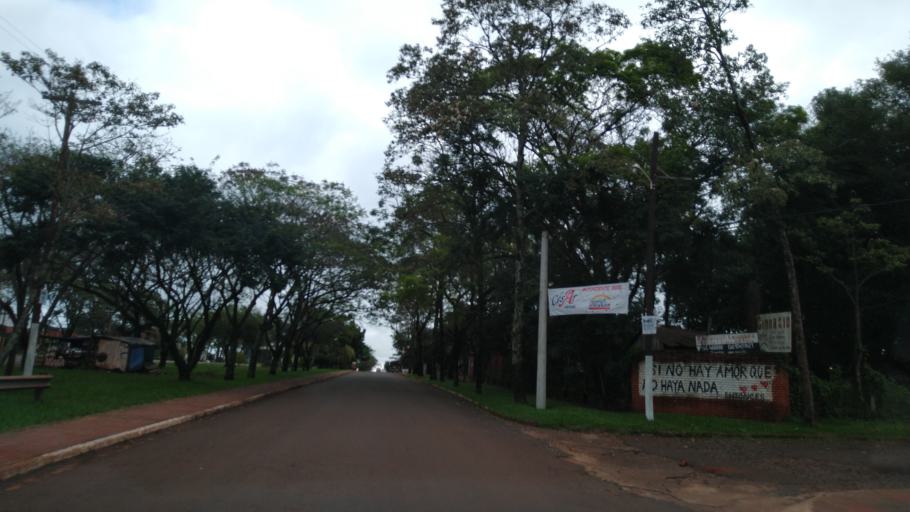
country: AR
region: Misiones
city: Jardin America
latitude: -27.0450
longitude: -55.2390
